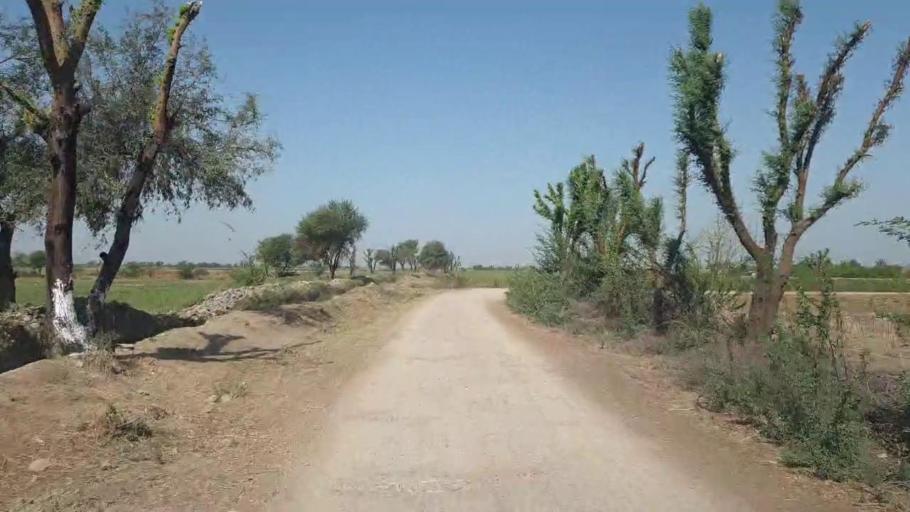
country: PK
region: Sindh
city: Kunri
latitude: 25.3015
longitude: 69.6181
